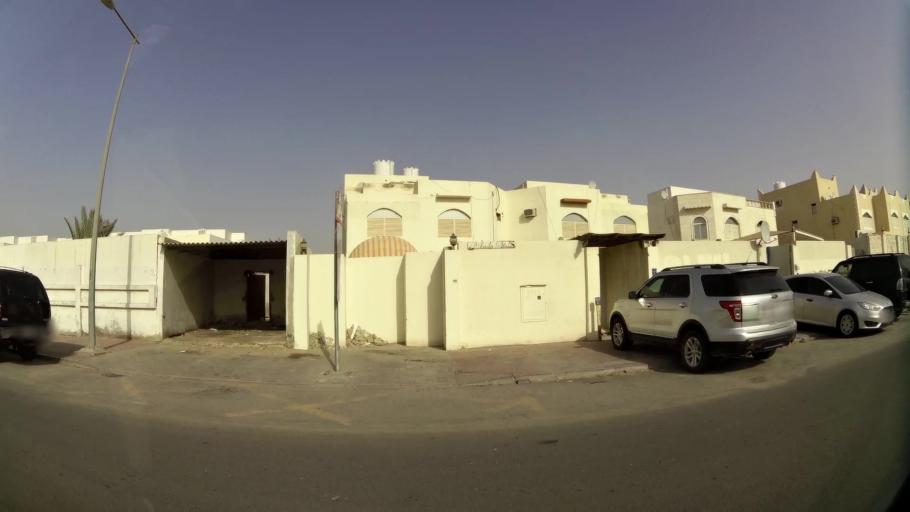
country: QA
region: Baladiyat ar Rayyan
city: Ar Rayyan
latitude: 25.2359
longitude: 51.4367
